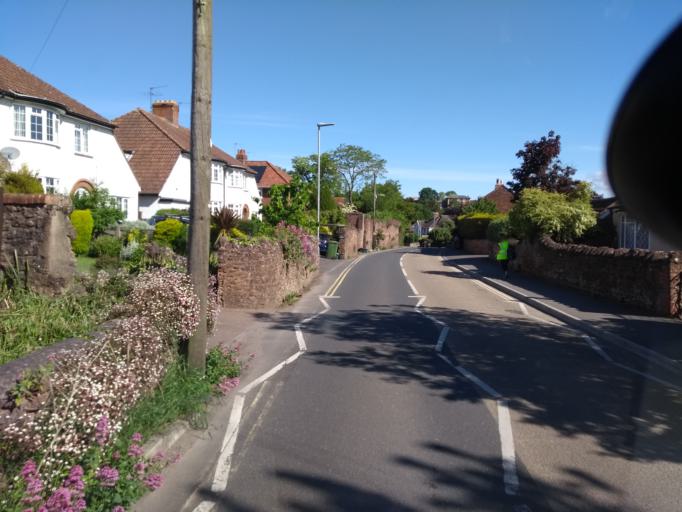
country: GB
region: England
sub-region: Somerset
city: Bridgwater
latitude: 51.1323
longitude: -3.0225
